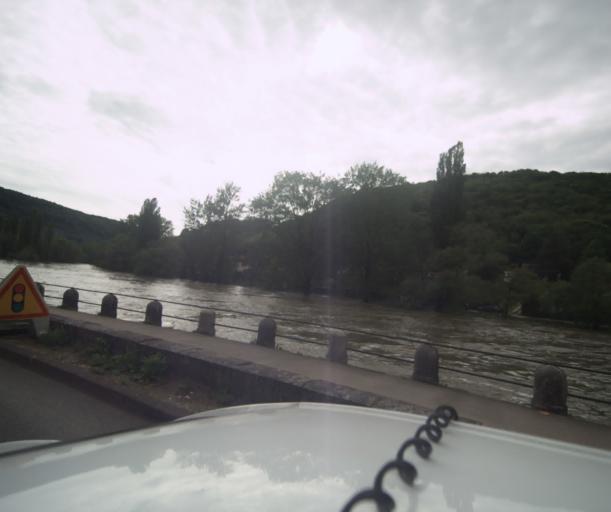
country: FR
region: Franche-Comte
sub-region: Departement du Doubs
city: Besancon
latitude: 47.2255
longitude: 6.0321
